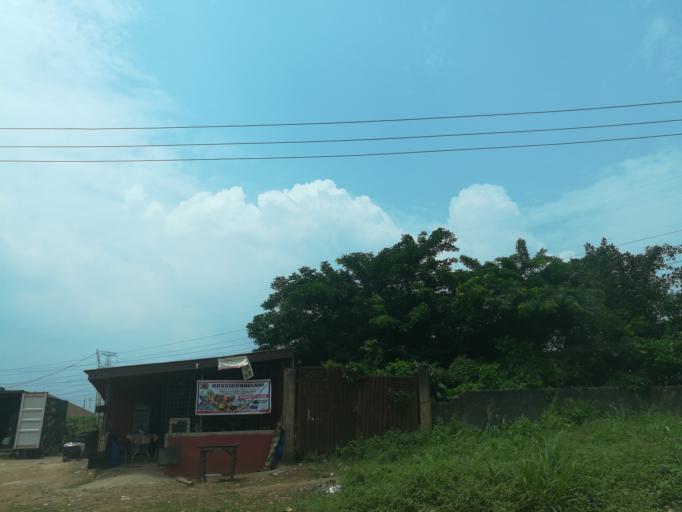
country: NG
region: Lagos
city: Ikorodu
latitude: 6.6073
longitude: 3.5881
